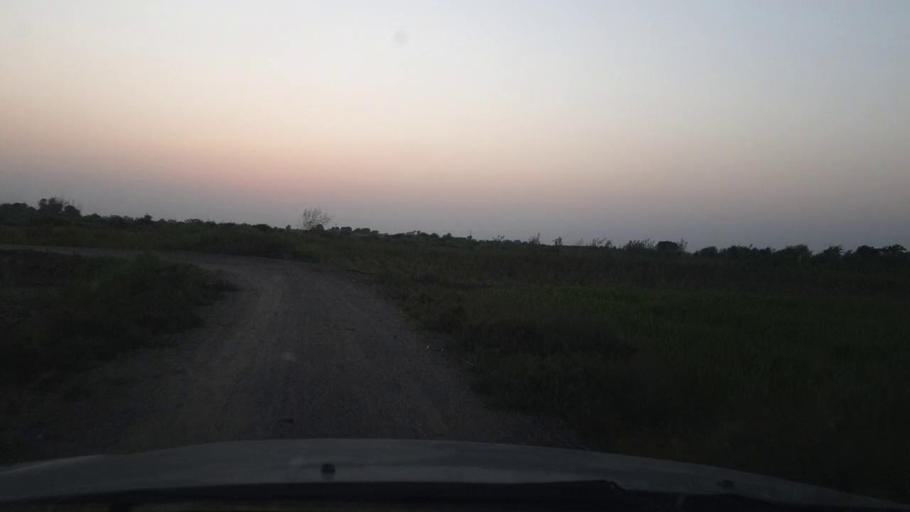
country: PK
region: Sindh
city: Digri
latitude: 25.1178
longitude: 68.9999
